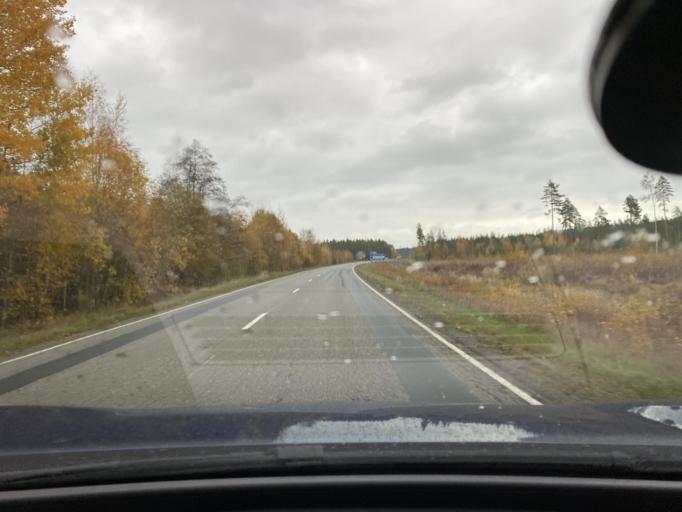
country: FI
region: Satakunta
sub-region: Rauma
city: Saekylae
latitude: 61.0459
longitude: 22.4174
